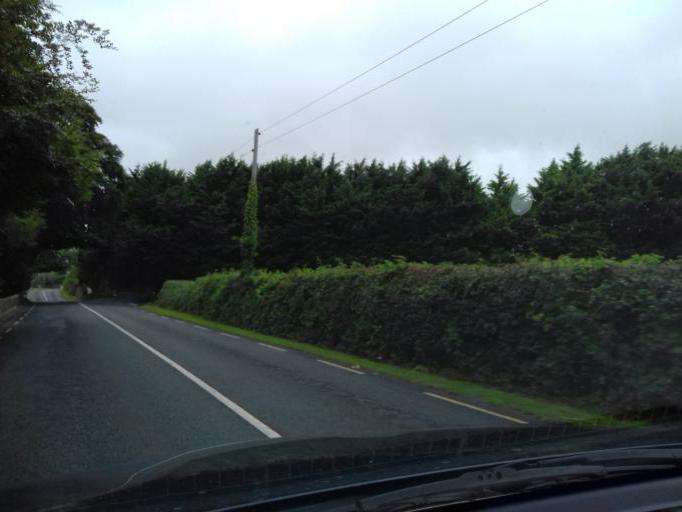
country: IE
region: Leinster
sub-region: County Carlow
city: Bagenalstown
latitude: 52.7142
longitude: -6.9586
